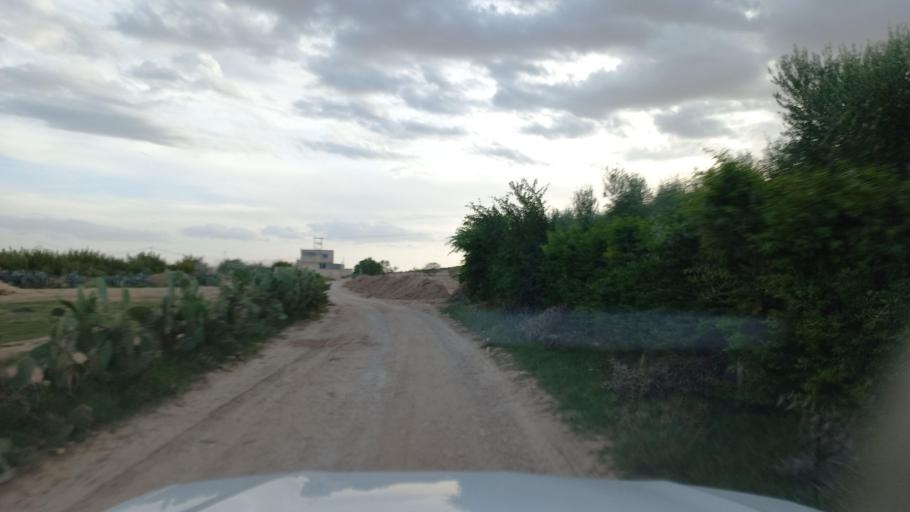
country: TN
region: Al Qasrayn
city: Sbiba
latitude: 35.4274
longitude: 9.0974
